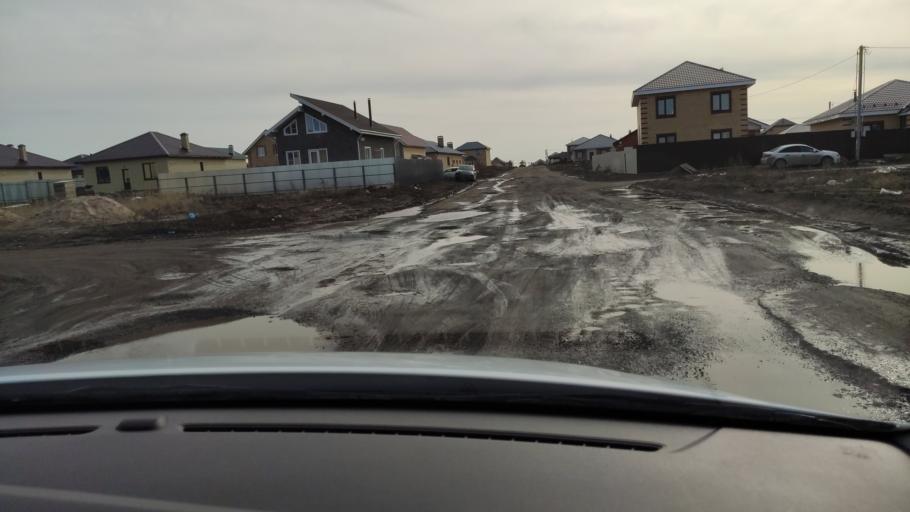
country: RU
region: Tatarstan
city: Stolbishchi
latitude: 55.7199
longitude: 49.3335
